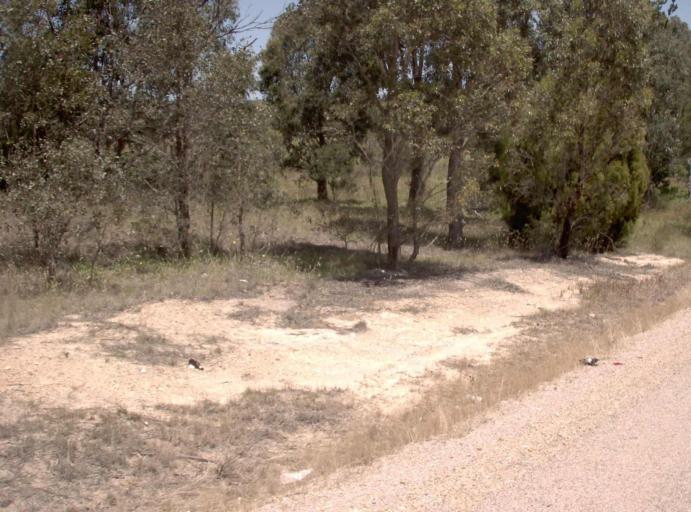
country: AU
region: Victoria
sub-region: East Gippsland
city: Bairnsdale
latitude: -37.7602
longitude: 147.7050
